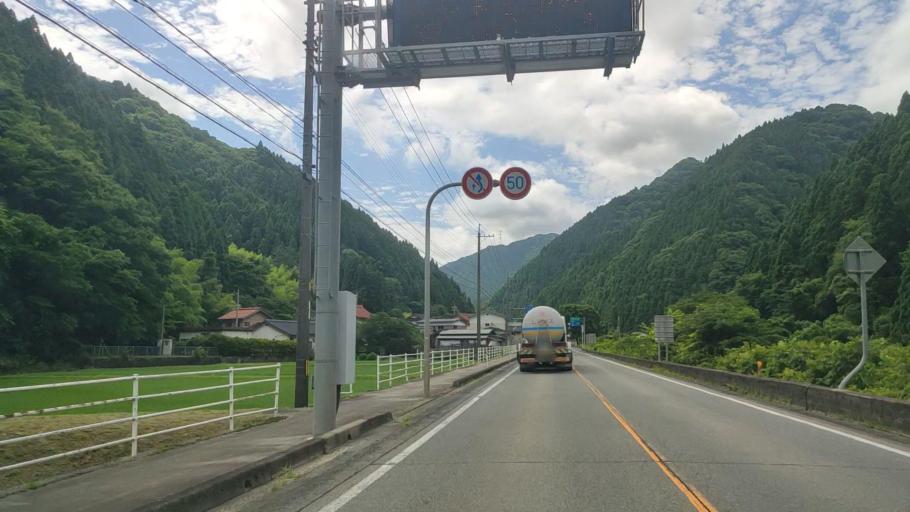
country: JP
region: Tottori
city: Yonago
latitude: 35.2299
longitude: 133.4431
